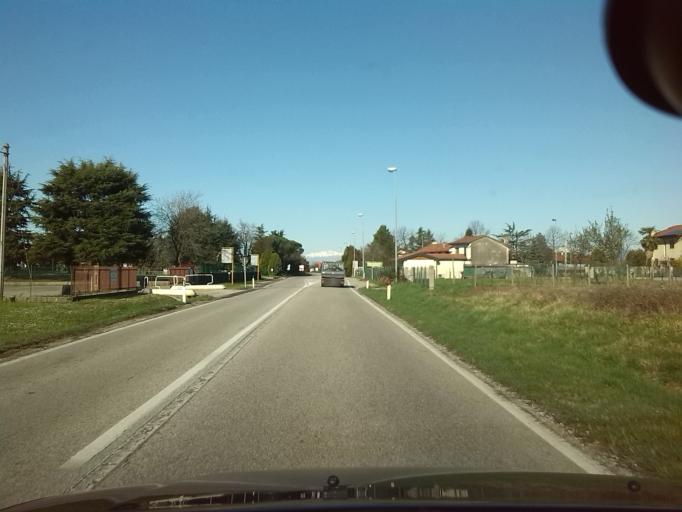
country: IT
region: Friuli Venezia Giulia
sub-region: Provincia di Udine
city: Moimacco
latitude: 46.0856
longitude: 13.3684
